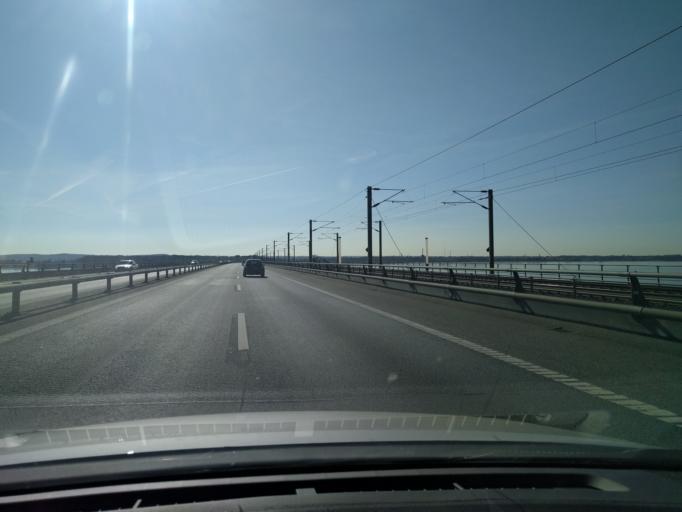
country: DK
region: South Denmark
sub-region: Nyborg Kommune
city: Nyborg
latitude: 55.3115
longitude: 10.9003
